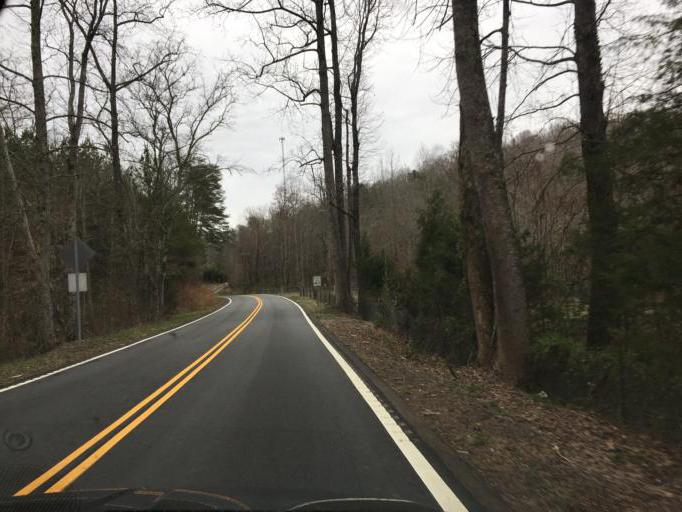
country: US
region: South Carolina
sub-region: Greenville County
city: Travelers Rest
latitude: 34.9382
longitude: -82.5157
